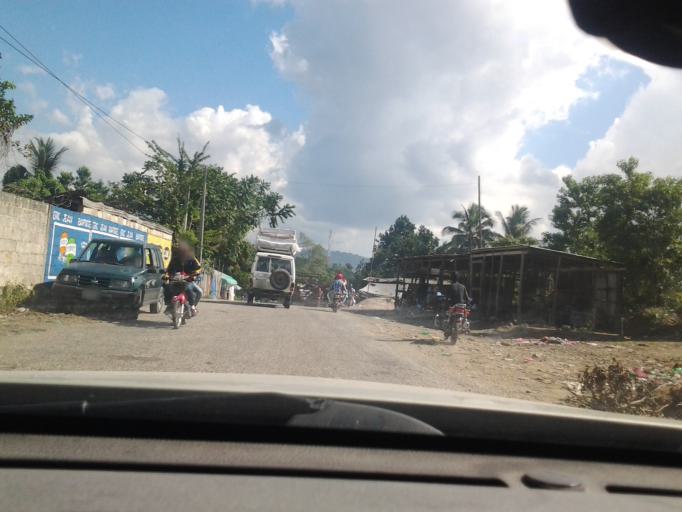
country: HT
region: Ouest
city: Leogane
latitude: 18.3983
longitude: -72.6372
